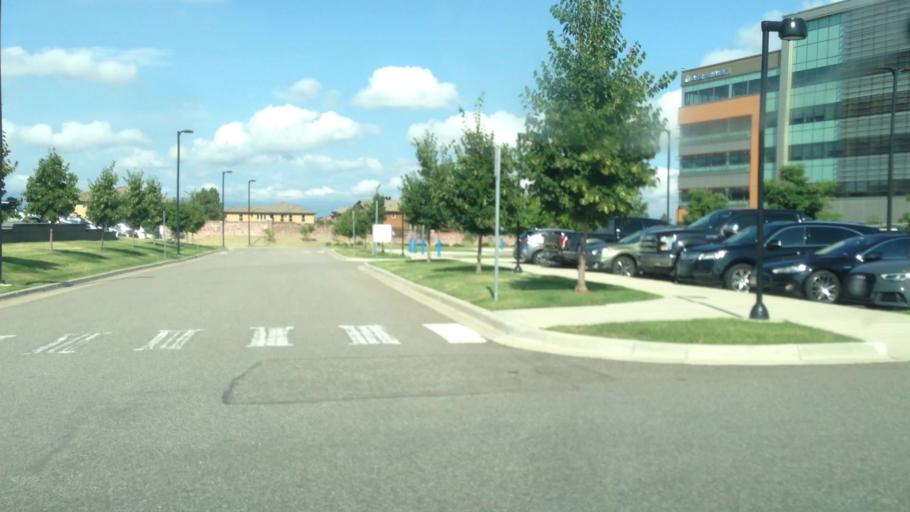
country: US
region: Colorado
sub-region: Douglas County
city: Meridian
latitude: 39.5441
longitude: -104.8716
